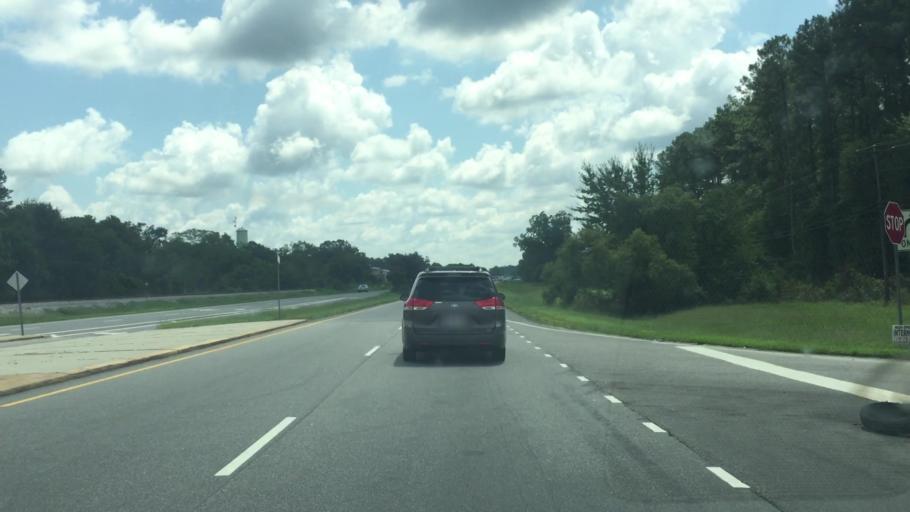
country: US
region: North Carolina
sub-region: Scotland County
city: Laurel Hill
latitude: 34.8106
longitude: -79.5542
